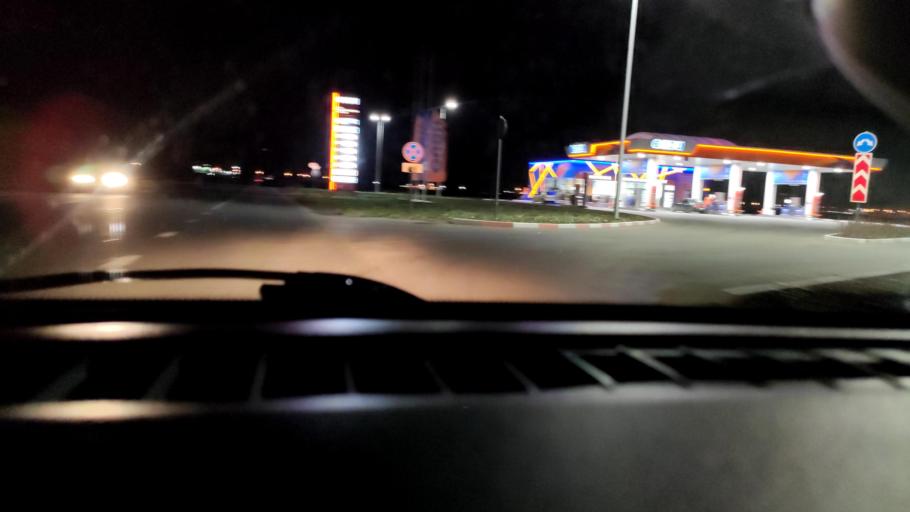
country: RU
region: Samara
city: Samara
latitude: 53.1295
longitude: 50.1540
